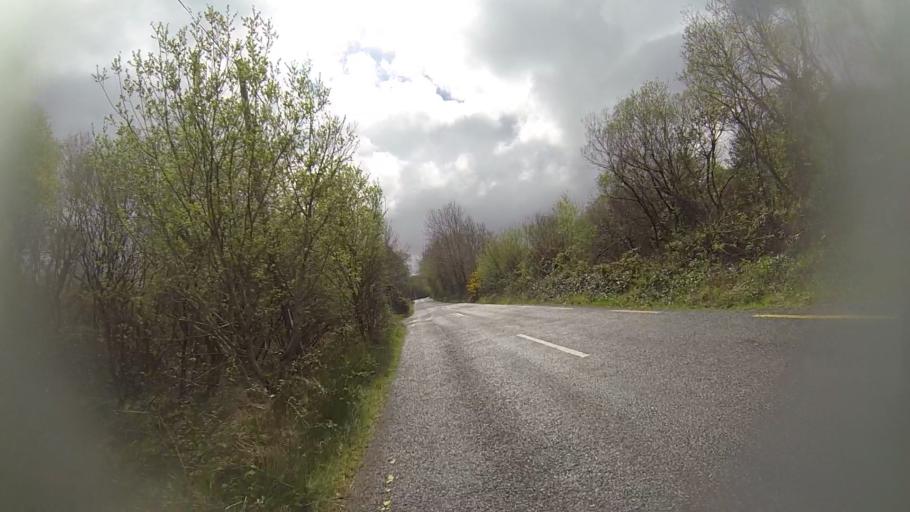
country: IE
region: Munster
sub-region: Ciarrai
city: Killorglin
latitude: 51.8413
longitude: -9.8932
